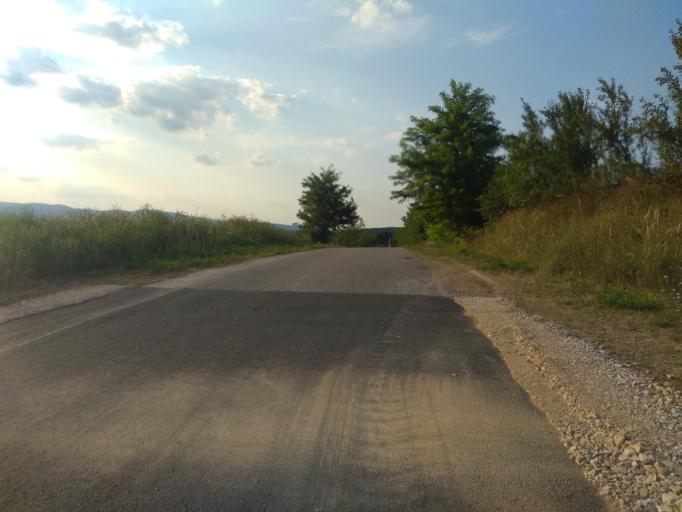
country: HU
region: Borsod-Abauj-Zemplen
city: Nyekladhaza
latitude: 47.9822
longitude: 20.7912
